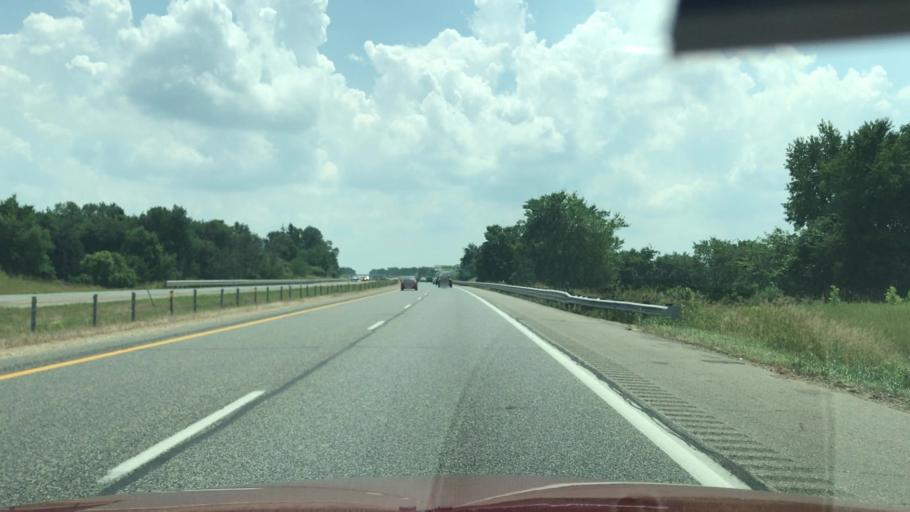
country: US
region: Michigan
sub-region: Allegan County
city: Otsego
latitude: 42.5487
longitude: -85.6622
